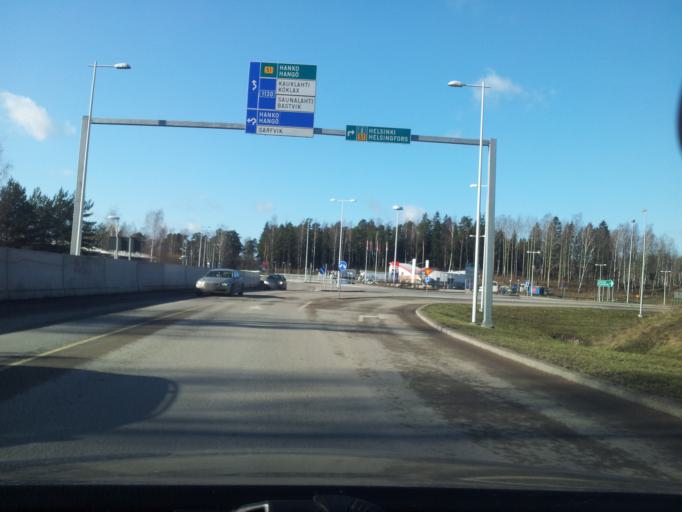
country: FI
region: Uusimaa
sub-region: Helsinki
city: Espoo
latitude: 60.1565
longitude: 24.6299
